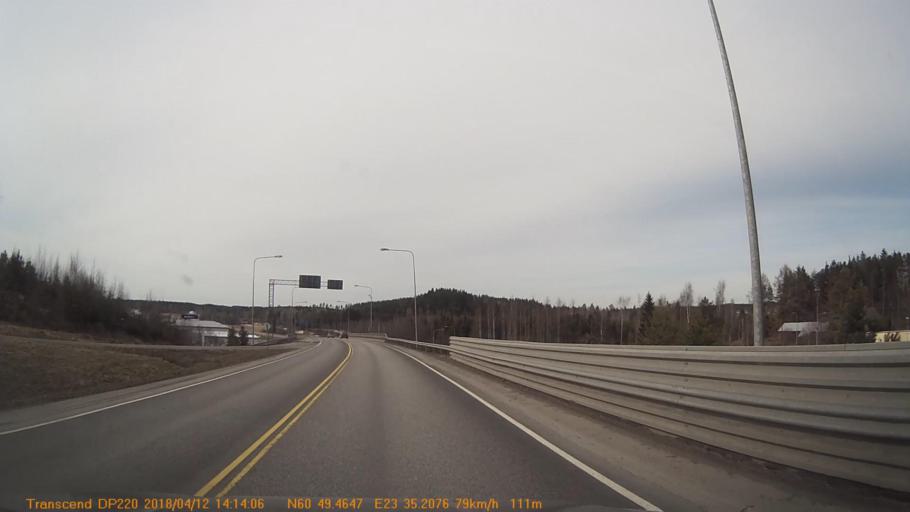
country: FI
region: Haeme
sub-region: Forssa
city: Forssa
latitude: 60.8247
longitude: 23.5862
